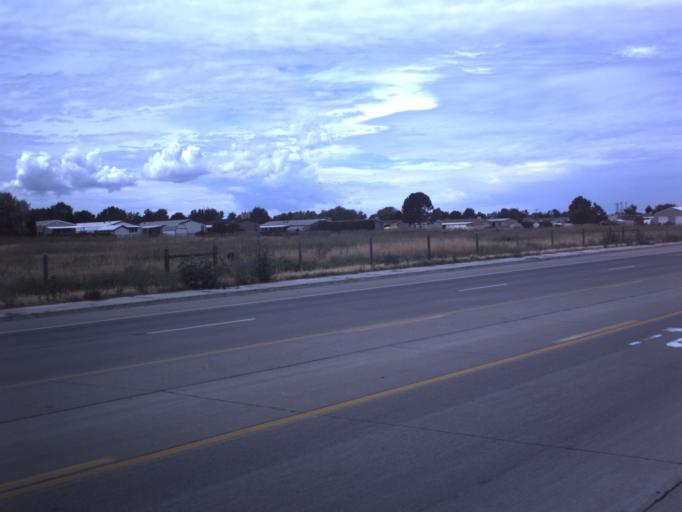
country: US
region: Utah
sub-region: Weber County
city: West Haven
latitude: 41.1974
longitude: -112.0373
